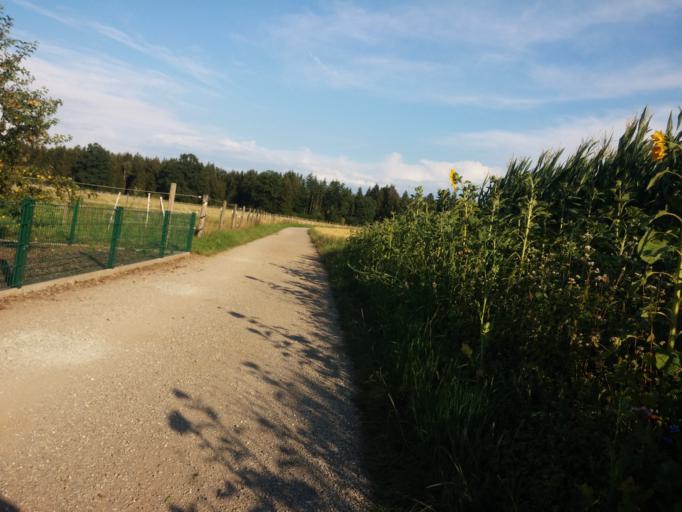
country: DE
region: Bavaria
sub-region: Upper Bavaria
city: Grasbrunn
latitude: 48.0728
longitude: 11.7531
